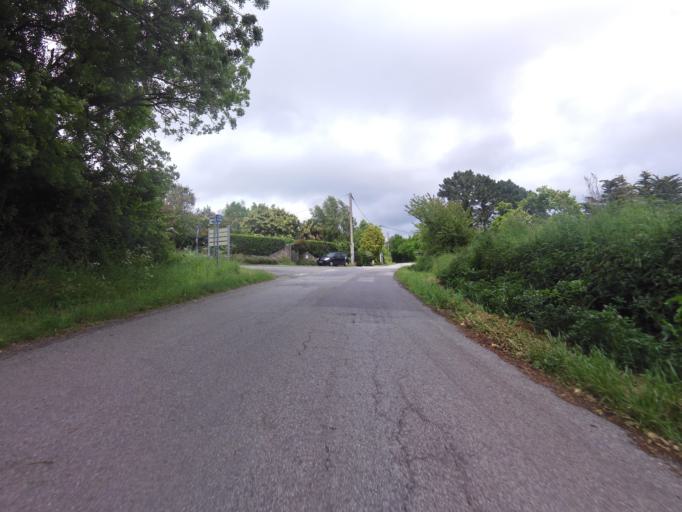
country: FR
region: Brittany
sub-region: Departement du Morbihan
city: Baden
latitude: 47.6050
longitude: -2.9376
